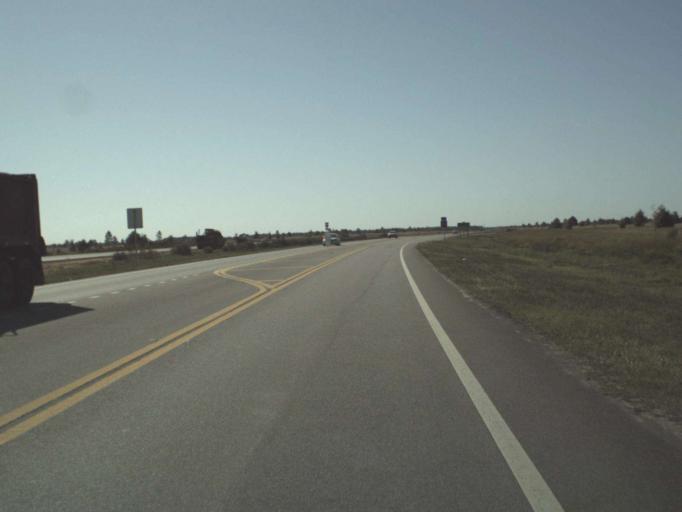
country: US
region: Florida
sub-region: Walton County
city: Freeport
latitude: 30.5550
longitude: -86.1065
